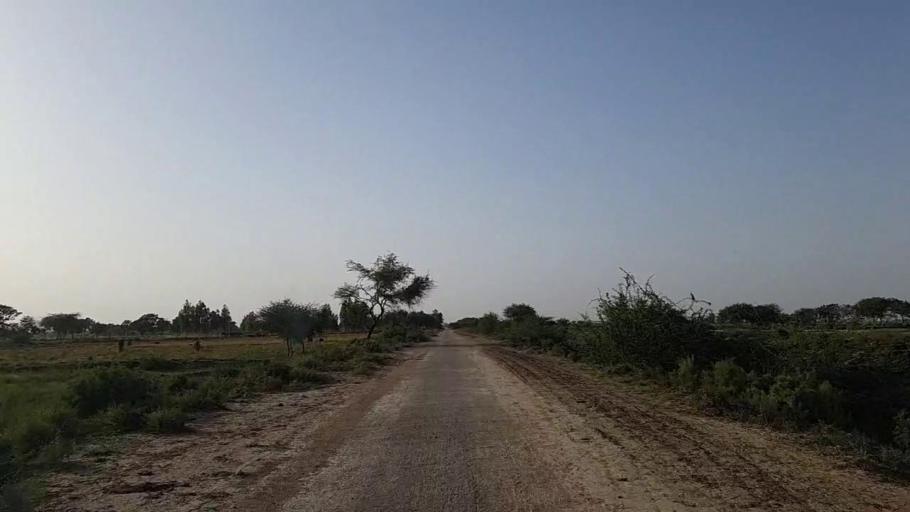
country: PK
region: Sindh
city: Jati
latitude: 24.3265
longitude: 68.1628
